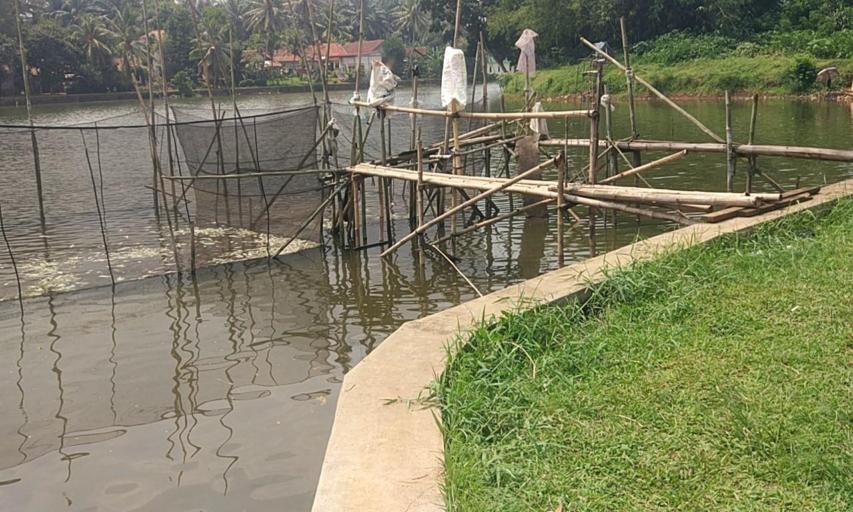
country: ID
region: West Java
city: Ciampea
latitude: -6.5302
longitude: 106.7277
